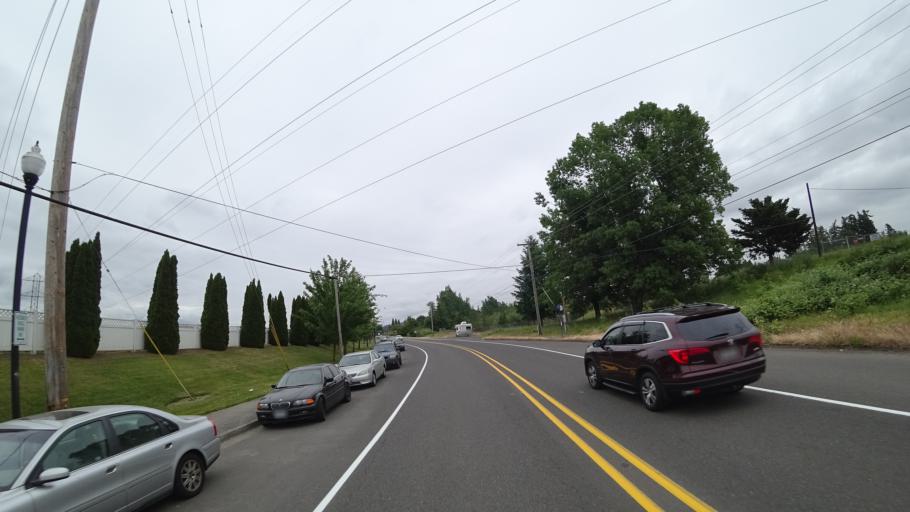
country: US
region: Oregon
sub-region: Multnomah County
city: Fairview
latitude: 45.5425
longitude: -122.4412
